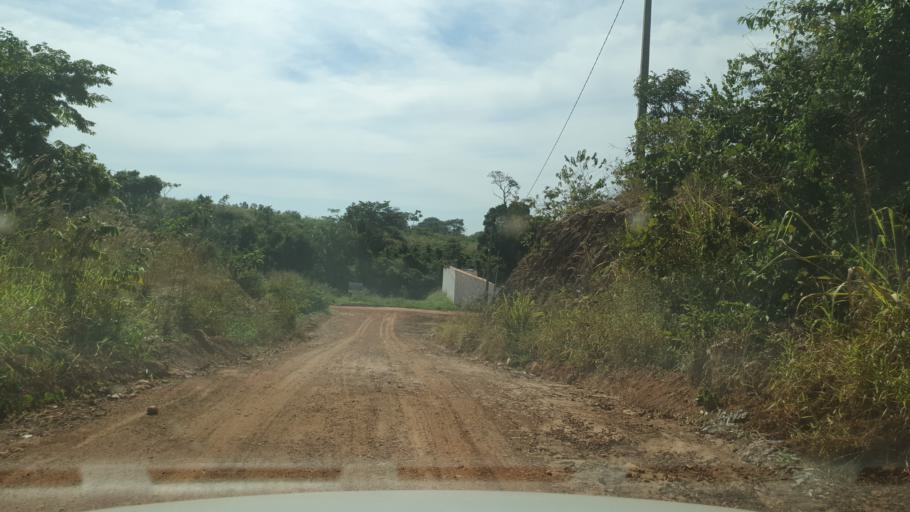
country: BR
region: Mato Grosso
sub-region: Pontes E Lacerda
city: Pontes e Lacerda
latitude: -15.2541
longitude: -59.3132
